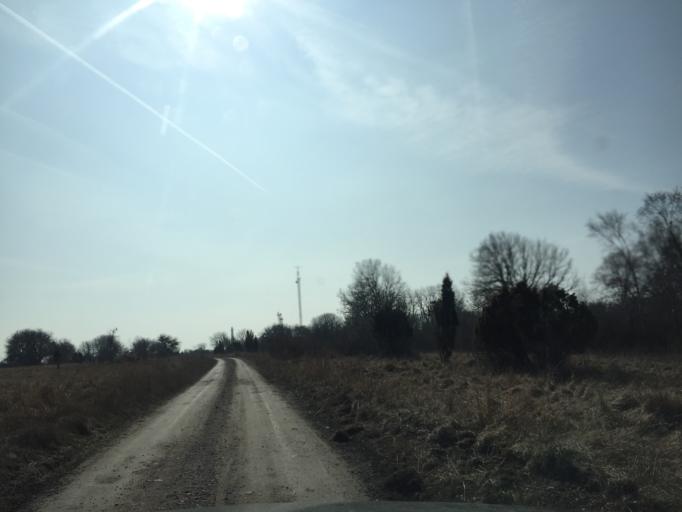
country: LV
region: Dundaga
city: Dundaga
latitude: 57.9206
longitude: 22.0602
